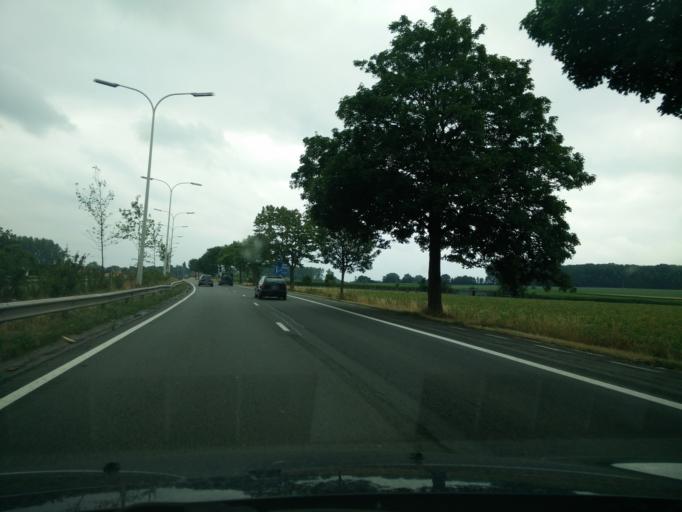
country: BE
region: Flanders
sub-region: Provincie Oost-Vlaanderen
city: Zingem
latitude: 50.9057
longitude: 3.6161
